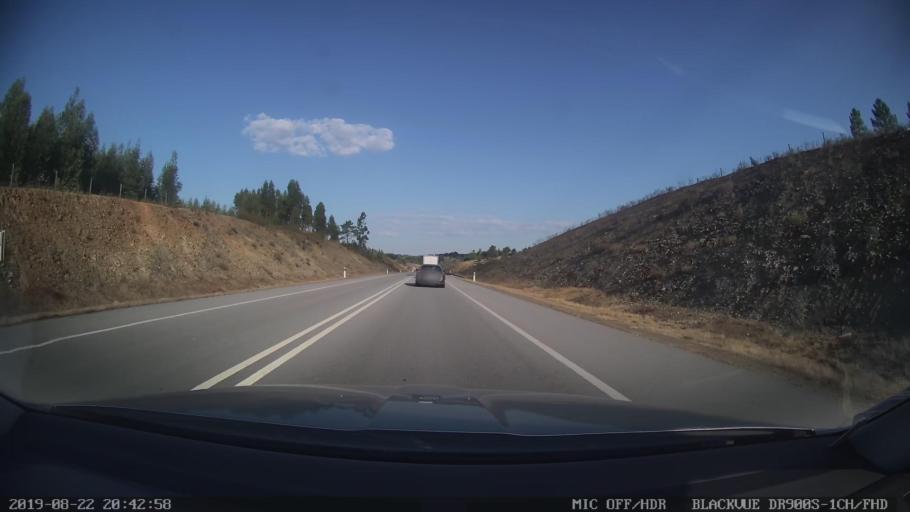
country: PT
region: Castelo Branco
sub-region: Proenca-A-Nova
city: Proenca-a-Nova
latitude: 39.6980
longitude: -7.8244
